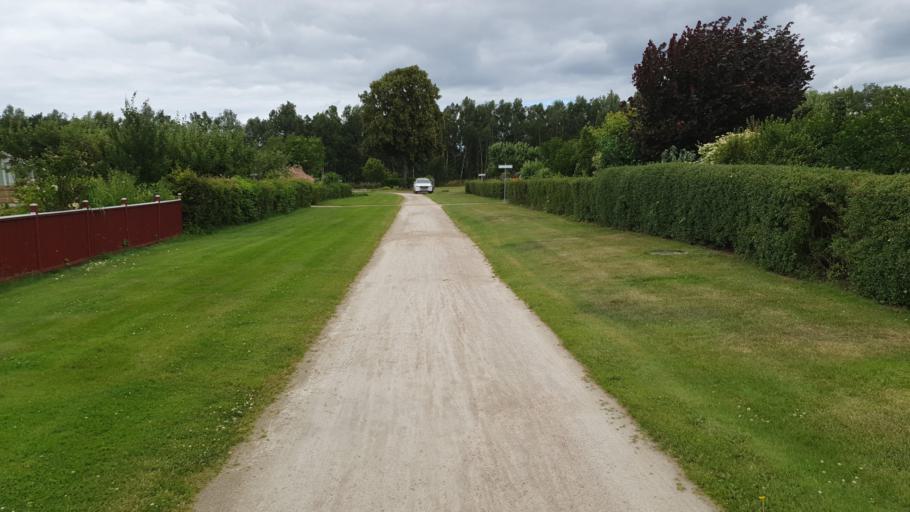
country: SE
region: Skane
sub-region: Kristianstads Kommun
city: Kristianstad
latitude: 56.0332
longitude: 14.1781
